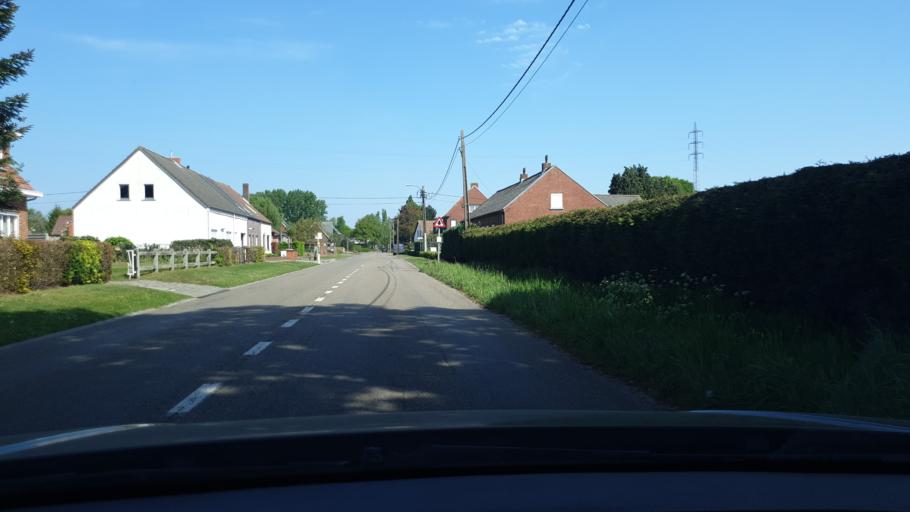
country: BE
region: Flanders
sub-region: Provincie Antwerpen
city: Geel
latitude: 51.1776
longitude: 5.0297
